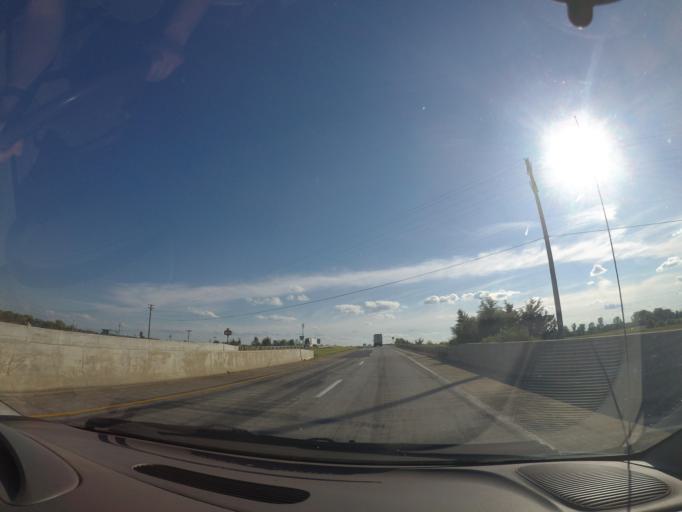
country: US
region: Ohio
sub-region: Henry County
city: Napoleon
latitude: 41.4085
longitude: -84.1318
